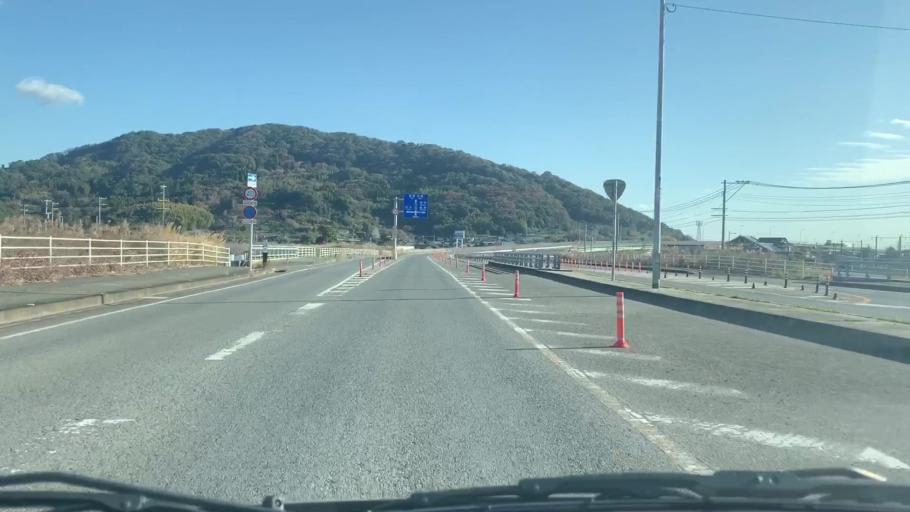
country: JP
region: Saga Prefecture
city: Kashima
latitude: 33.2203
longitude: 130.1476
